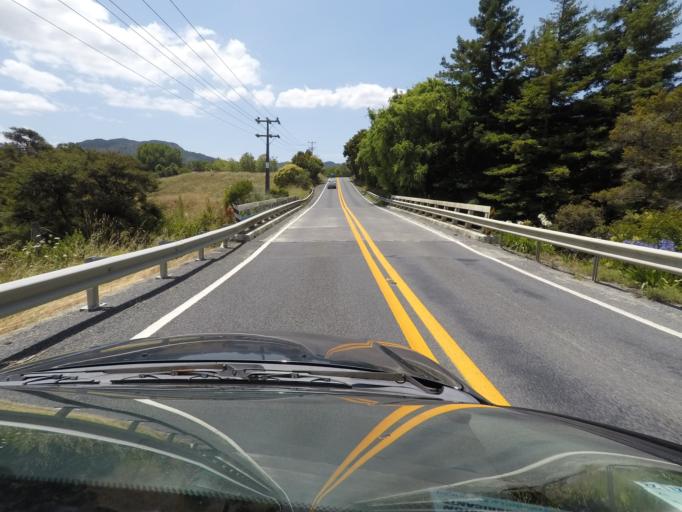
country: NZ
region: Auckland
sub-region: Auckland
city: Warkworth
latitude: -36.3287
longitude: 174.7321
